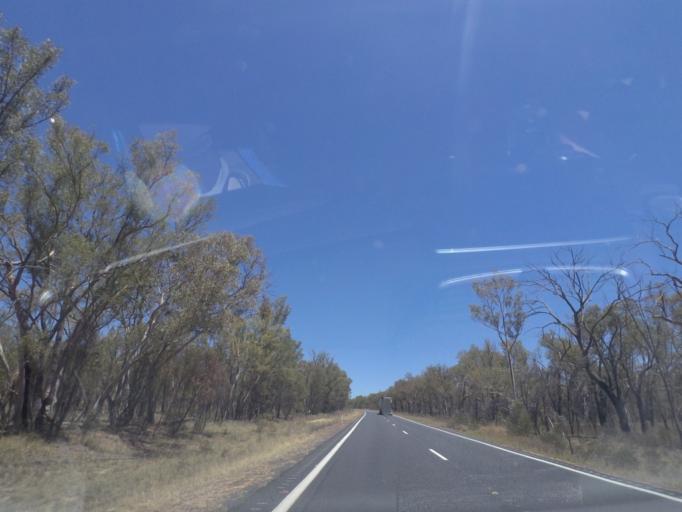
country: AU
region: New South Wales
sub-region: Warrumbungle Shire
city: Coonabarabran
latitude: -31.1760
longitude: 149.3579
